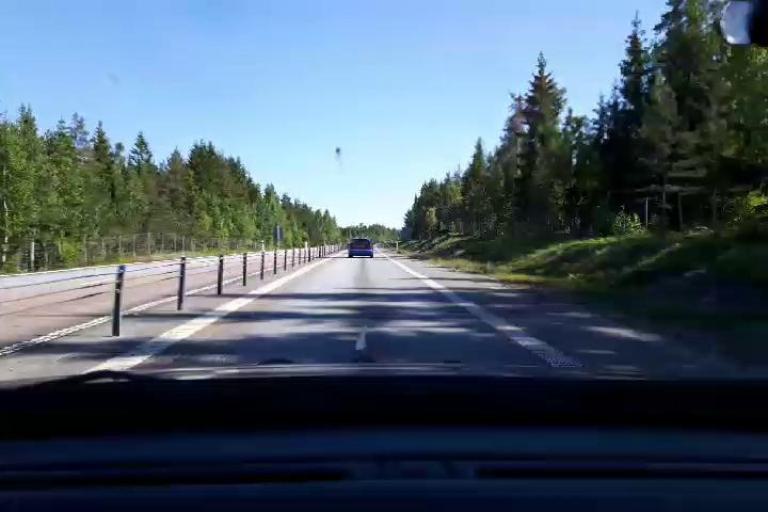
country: SE
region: Gaevleborg
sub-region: Gavle Kommun
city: Norrsundet
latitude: 60.8895
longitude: 17.0381
